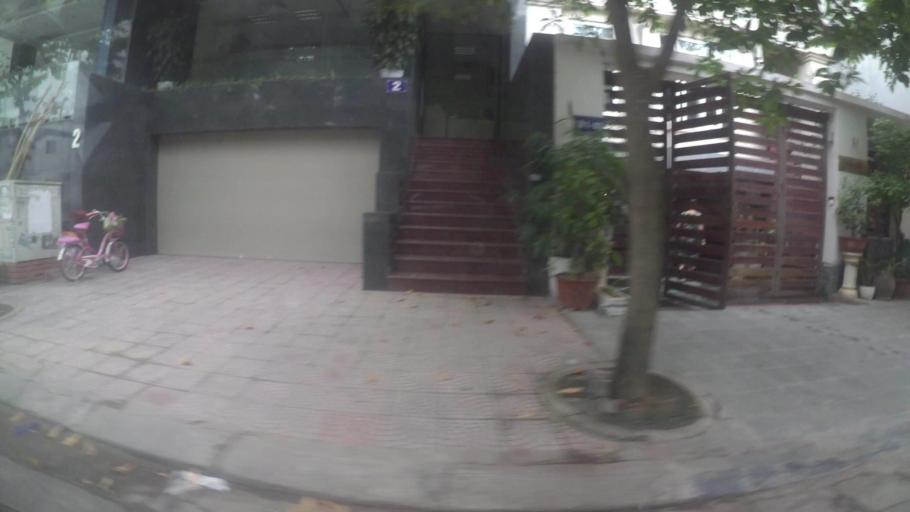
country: VN
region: Ha Noi
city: Cau Dien
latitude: 21.0335
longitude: 105.7622
